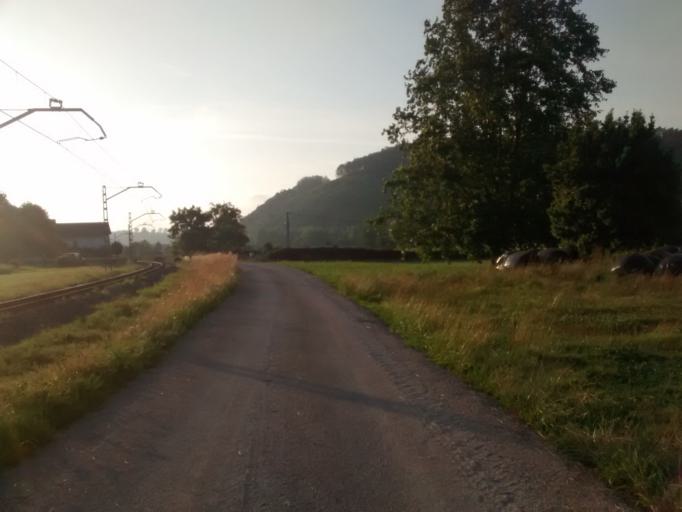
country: ES
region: Cantabria
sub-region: Provincia de Cantabria
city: Entrambasaguas
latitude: 43.3746
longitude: -3.7147
